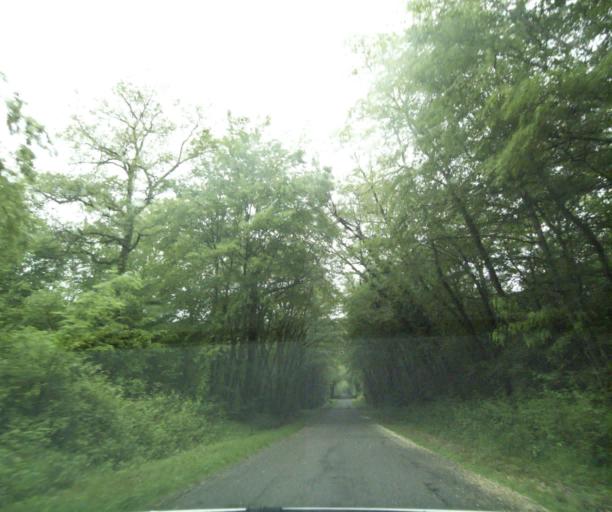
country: FR
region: Bourgogne
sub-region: Departement de Saone-et-Loire
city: Paray-le-Monial
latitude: 46.4212
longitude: 4.1921
